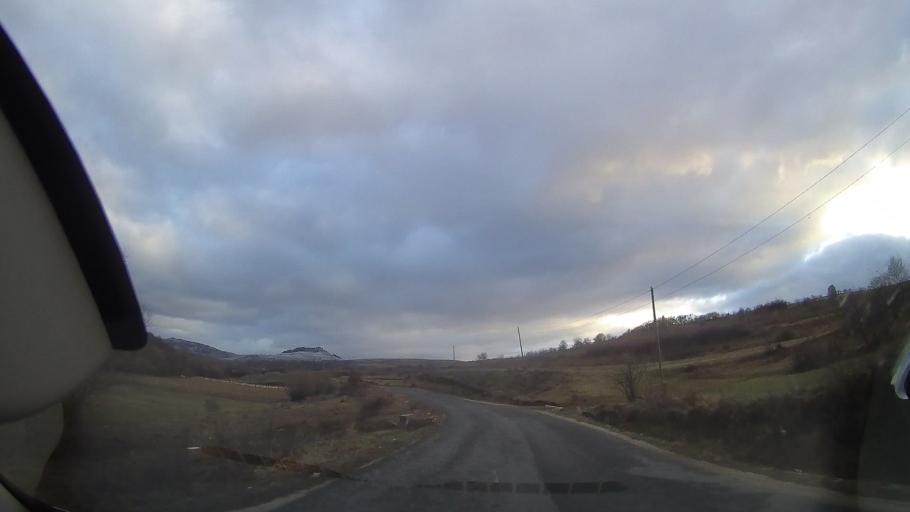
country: RO
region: Cluj
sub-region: Comuna Calatele
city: Calatele
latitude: 46.7873
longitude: 23.0132
